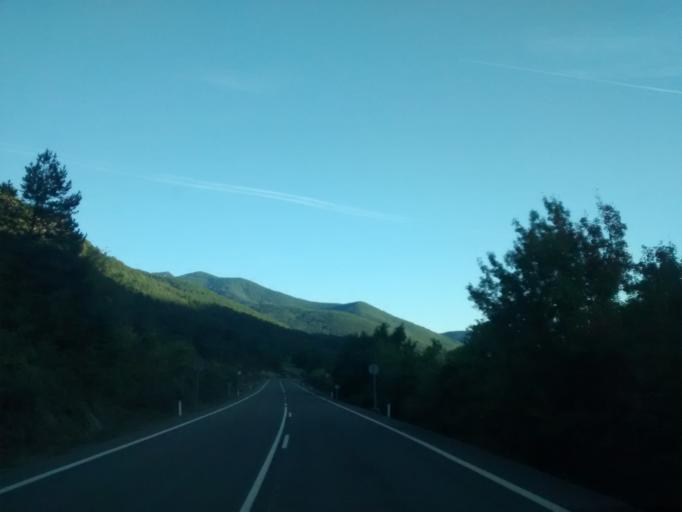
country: ES
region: Aragon
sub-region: Provincia de Huesca
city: Aragues del Puerto
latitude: 42.6921
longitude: -0.7379
